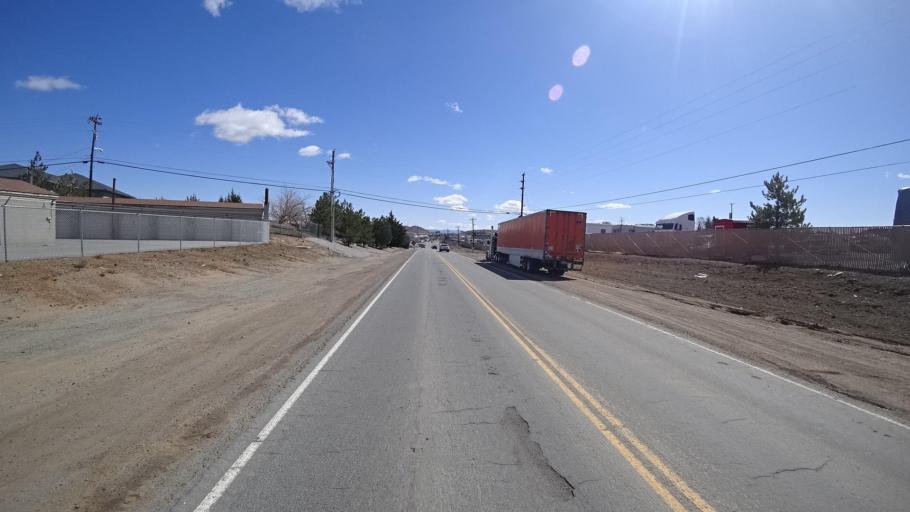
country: US
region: Nevada
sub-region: Washoe County
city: Golden Valley
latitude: 39.6009
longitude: -119.8461
